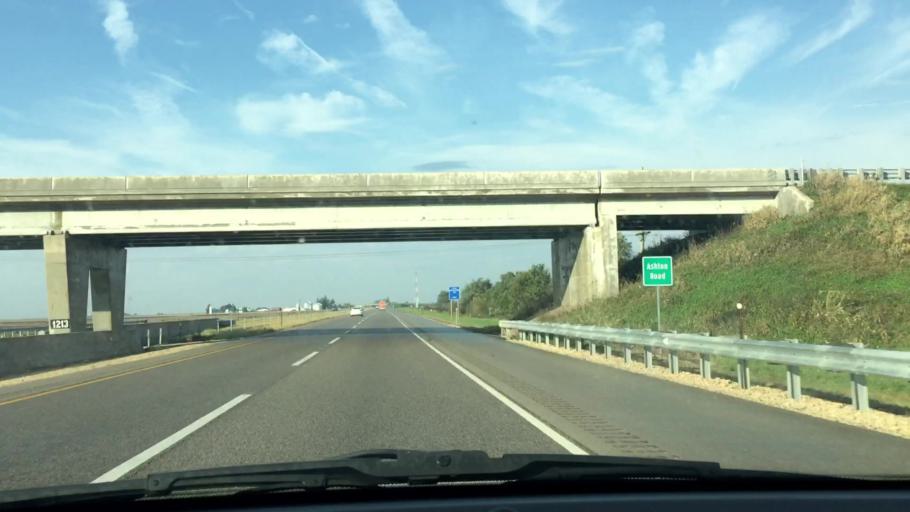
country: US
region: Illinois
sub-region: Lee County
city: Franklin Grove
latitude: 41.8584
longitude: -89.2074
